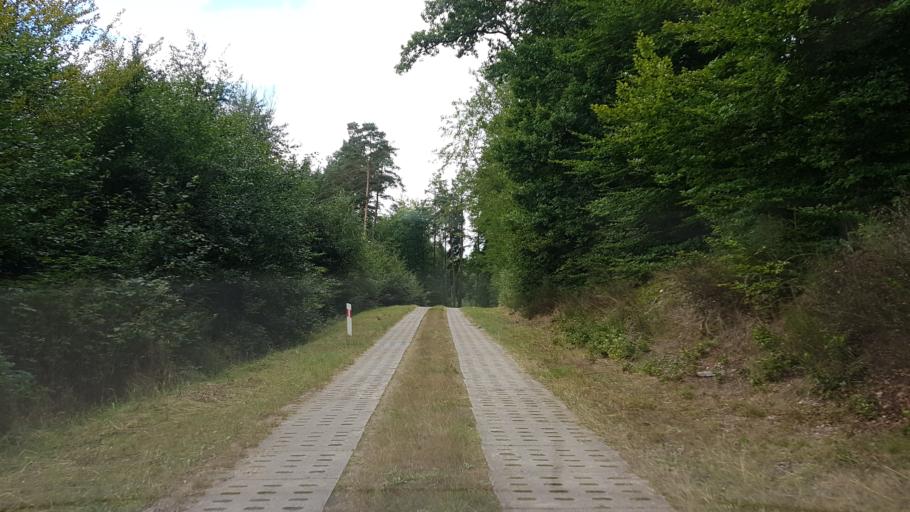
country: PL
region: West Pomeranian Voivodeship
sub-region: Powiat szczecinecki
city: Grzmiaca
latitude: 53.9660
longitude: 16.3929
